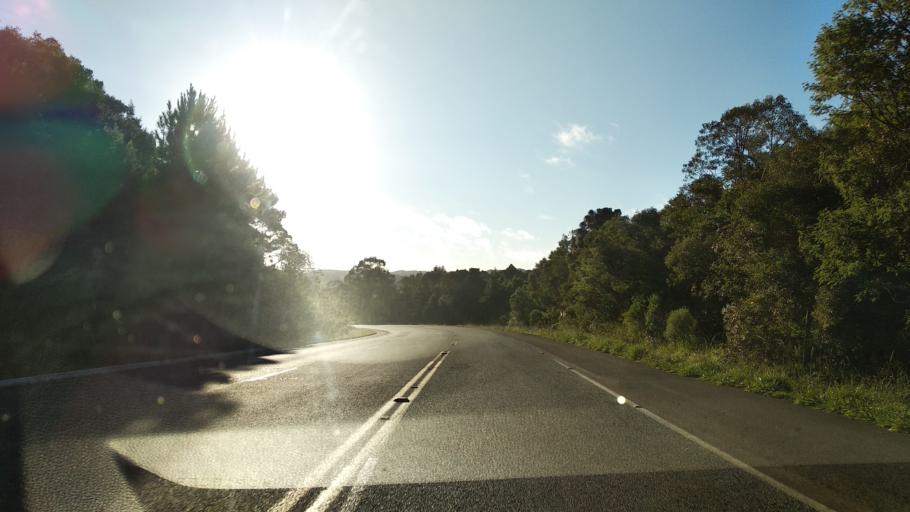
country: BR
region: Santa Catarina
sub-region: Correia Pinto
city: Correia Pinto
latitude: -27.6251
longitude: -50.6540
